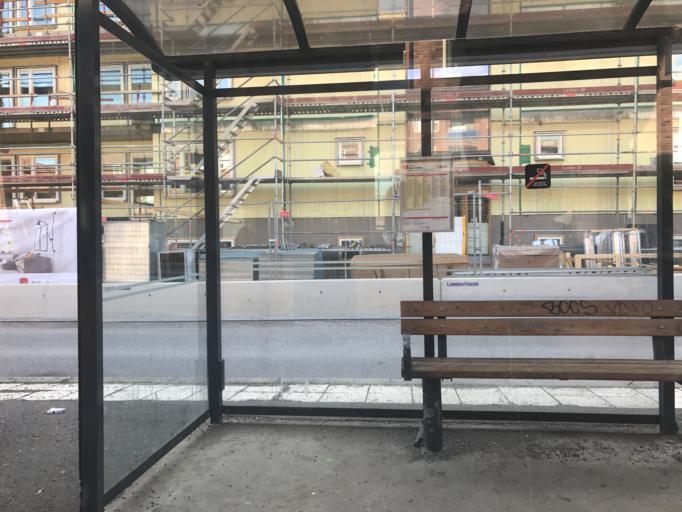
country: SE
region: OEstergoetland
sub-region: Norrkopings Kommun
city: Norrkoping
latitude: 58.5802
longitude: 16.1973
